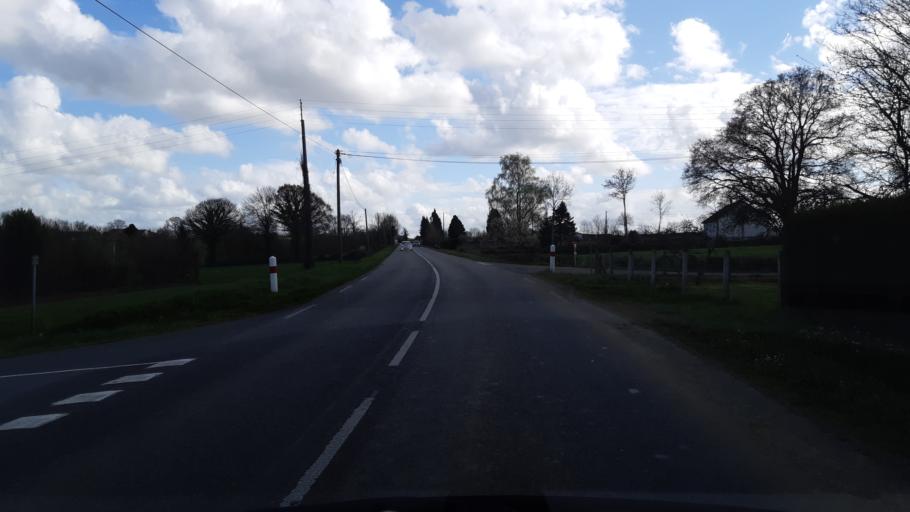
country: FR
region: Lower Normandy
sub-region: Departement de la Manche
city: Agneaux
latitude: 49.0587
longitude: -1.1333
